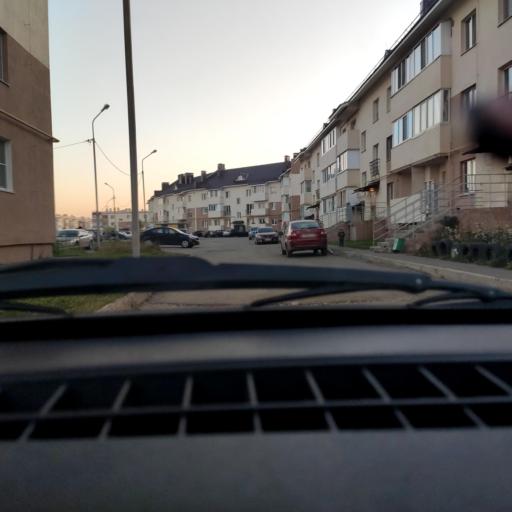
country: RU
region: Bashkortostan
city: Ufa
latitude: 54.8353
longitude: 56.1717
